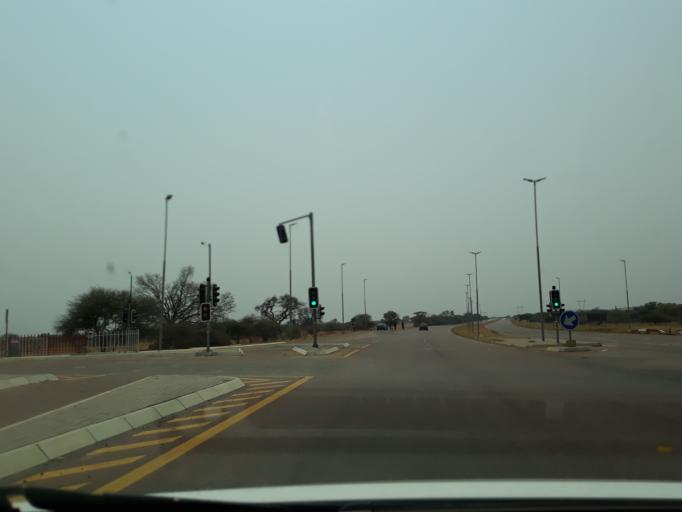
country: BW
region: Kgatleng
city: Mochudi
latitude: -24.3643
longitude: 26.0678
